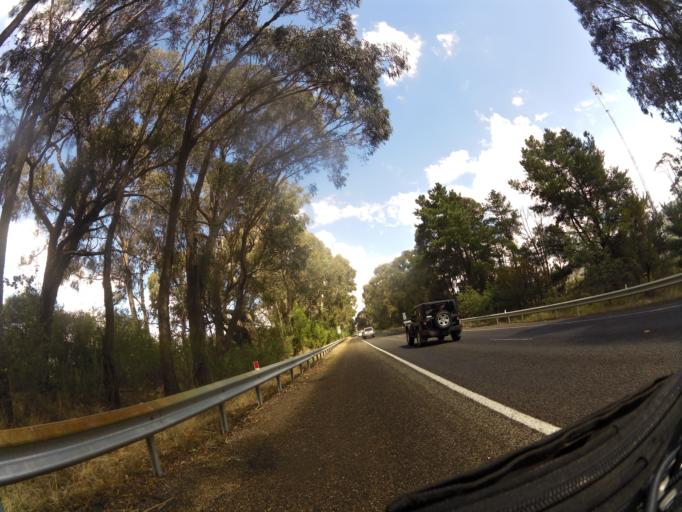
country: AU
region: Victoria
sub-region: Mansfield
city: Mansfield
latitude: -36.8309
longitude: 146.0085
